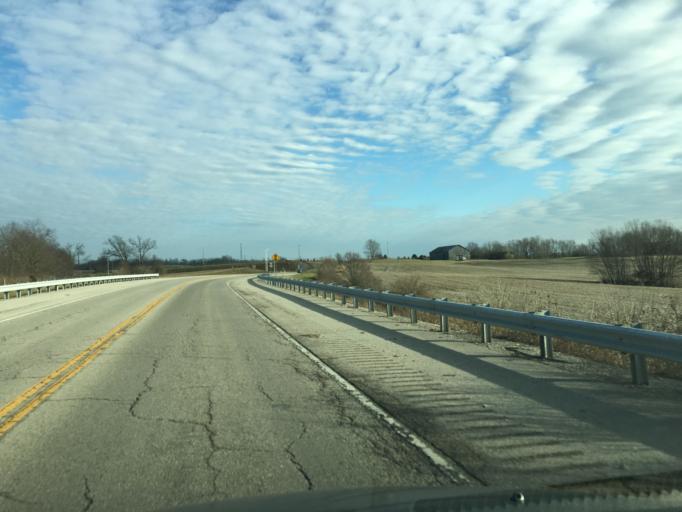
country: US
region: Kentucky
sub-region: Scott County
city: Georgetown
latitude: 38.2395
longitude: -84.5562
